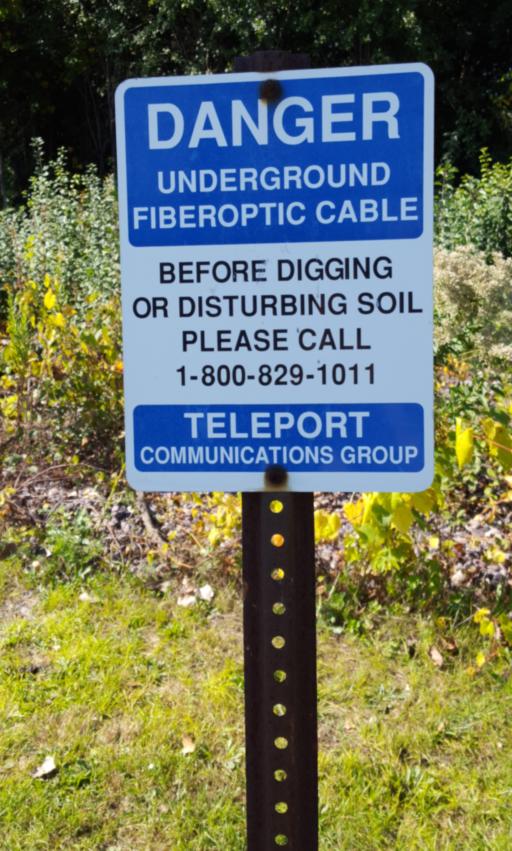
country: US
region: Illinois
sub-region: Cook County
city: Glenview
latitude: 42.0794
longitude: -87.7648
